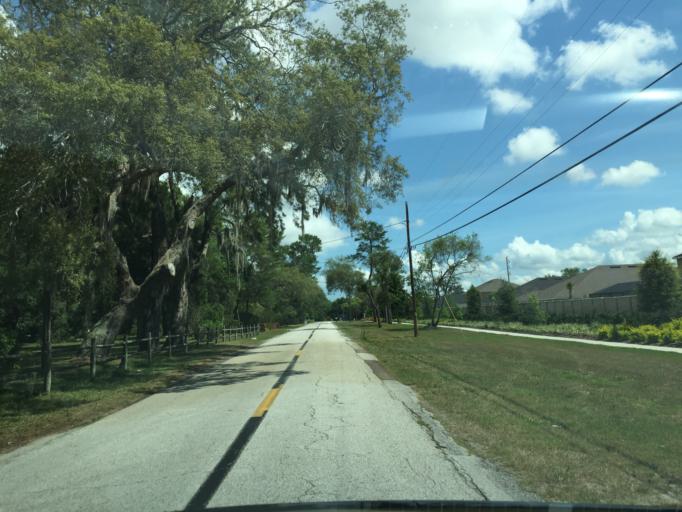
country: US
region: Florida
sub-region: Pinellas County
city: Saint George
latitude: 28.0538
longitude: -82.7431
